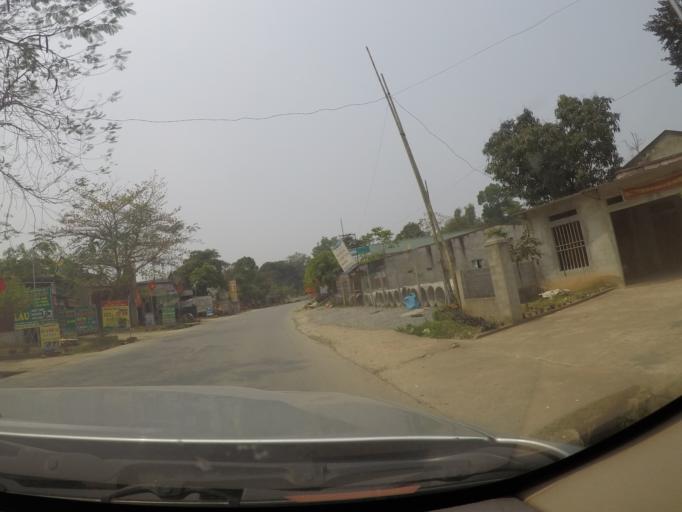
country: VN
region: Thanh Hoa
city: Thi Tran Ngoc Lac
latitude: 20.1255
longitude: 105.3944
